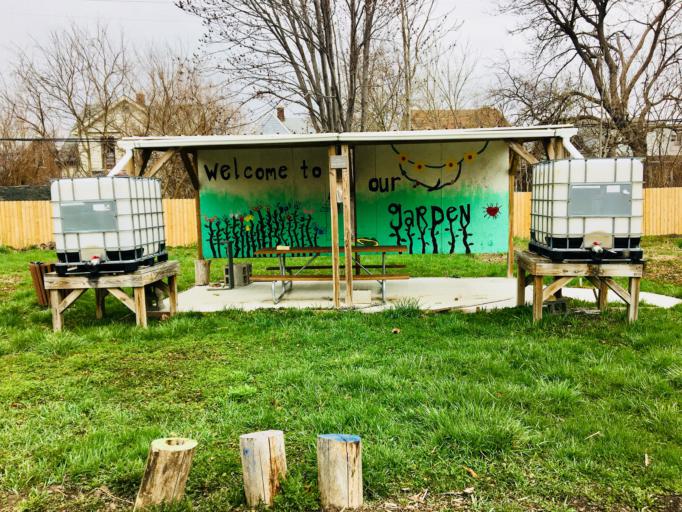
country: US
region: Michigan
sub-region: Wayne County
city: Grosse Pointe Park
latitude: 42.4126
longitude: -82.9880
